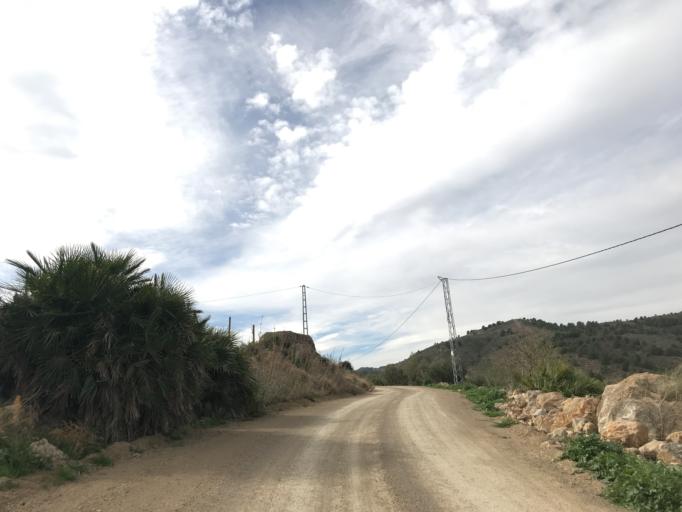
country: ES
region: Andalusia
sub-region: Provincia de Malaga
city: Ardales
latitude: 36.8780
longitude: -4.8741
